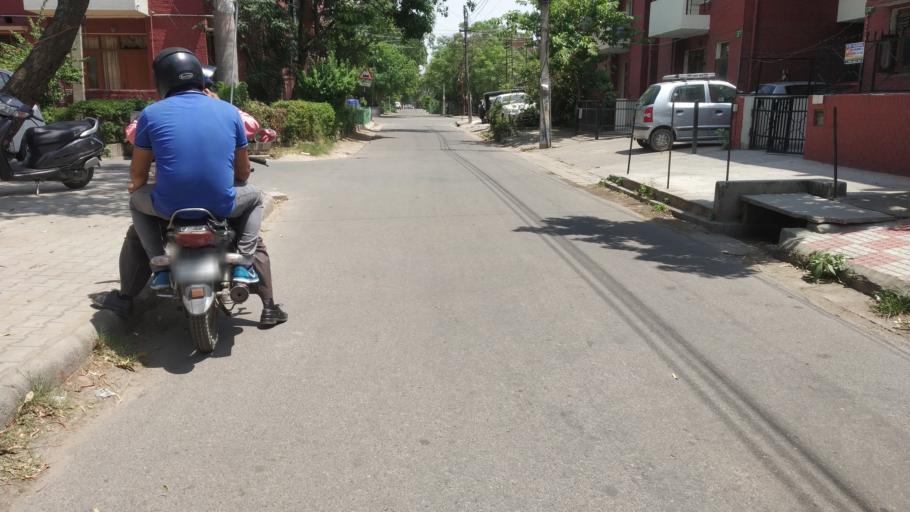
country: IN
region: Punjab
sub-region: Ajitgarh
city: Mohali
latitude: 30.7087
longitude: 76.7306
